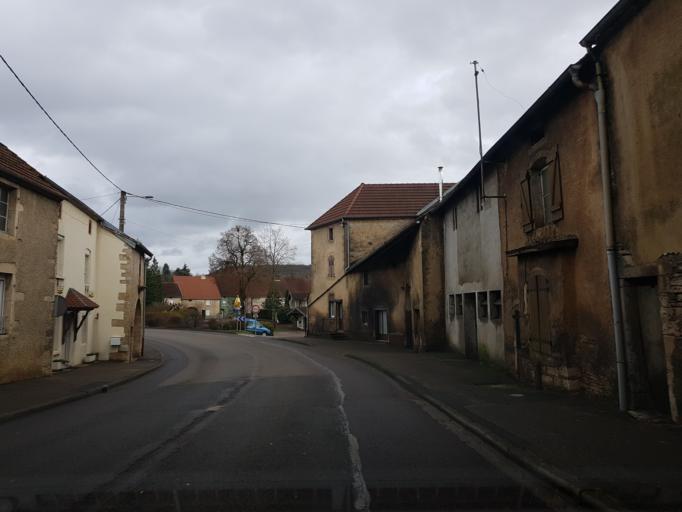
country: FR
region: Franche-Comte
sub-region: Departement de la Haute-Saone
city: Scey-sur-Saone-et-Saint-Albin
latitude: 47.7091
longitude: 5.8925
